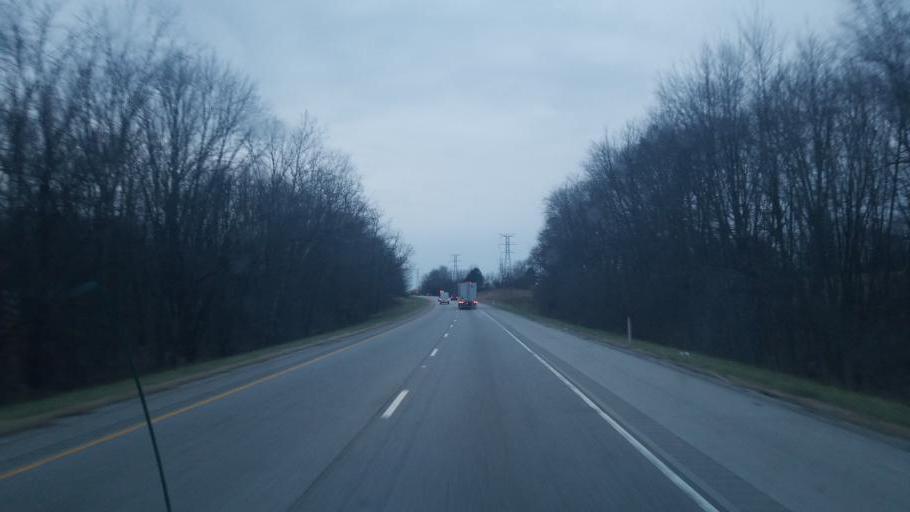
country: US
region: Indiana
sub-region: Vigo County
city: Seelyville
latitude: 39.4434
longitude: -87.2710
